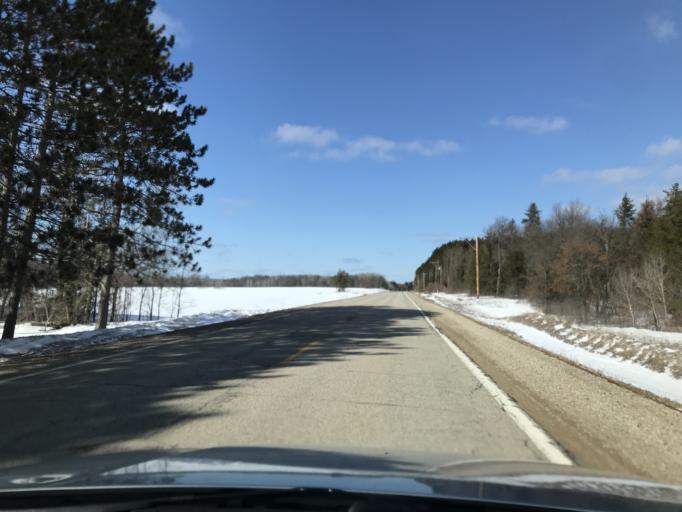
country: US
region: Wisconsin
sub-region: Marinette County
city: Peshtigo
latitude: 45.3201
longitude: -88.1021
